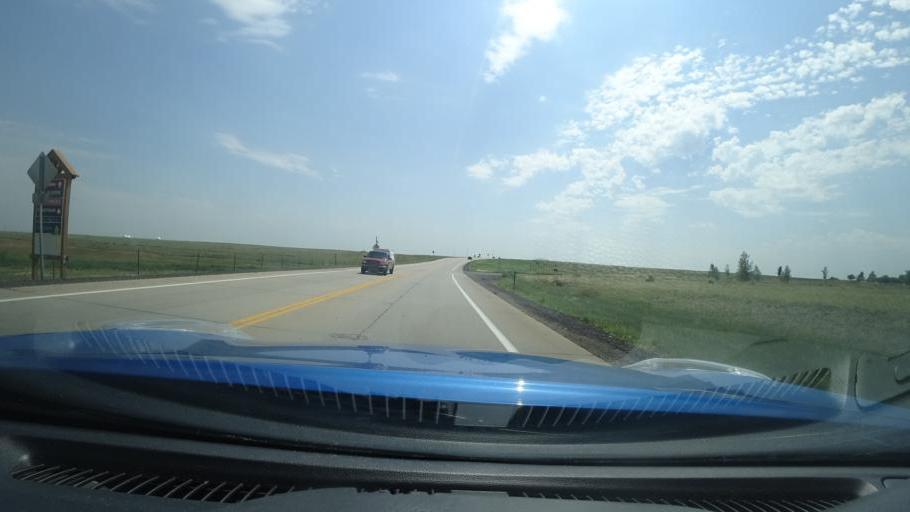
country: US
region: Colorado
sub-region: Adams County
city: Aurora
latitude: 39.6820
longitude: -104.7553
